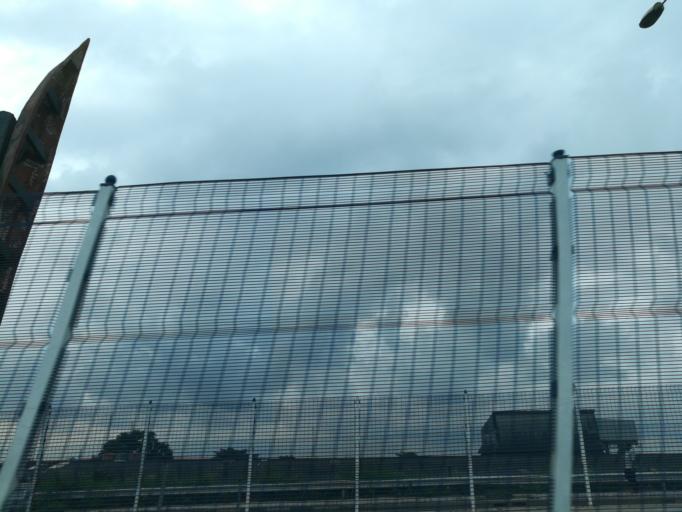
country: NG
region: Lagos
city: Ikeja
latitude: 6.5908
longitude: 3.3386
